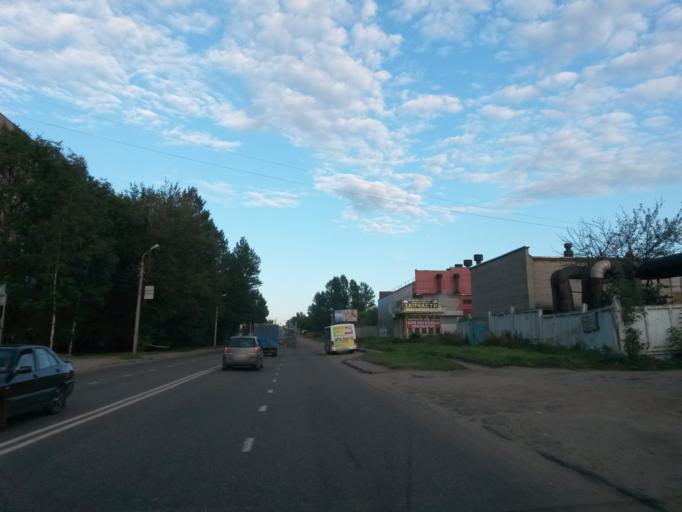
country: RU
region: Jaroslavl
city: Yaroslavl
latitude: 57.5788
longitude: 39.8363
